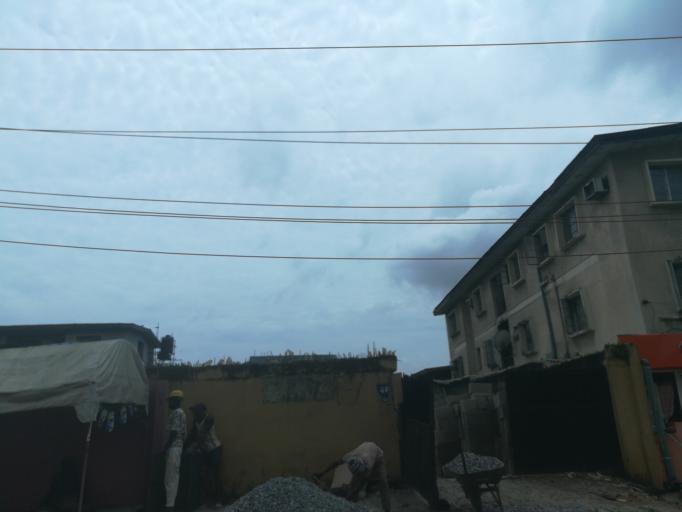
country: NG
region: Lagos
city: Somolu
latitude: 6.5277
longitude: 3.3867
